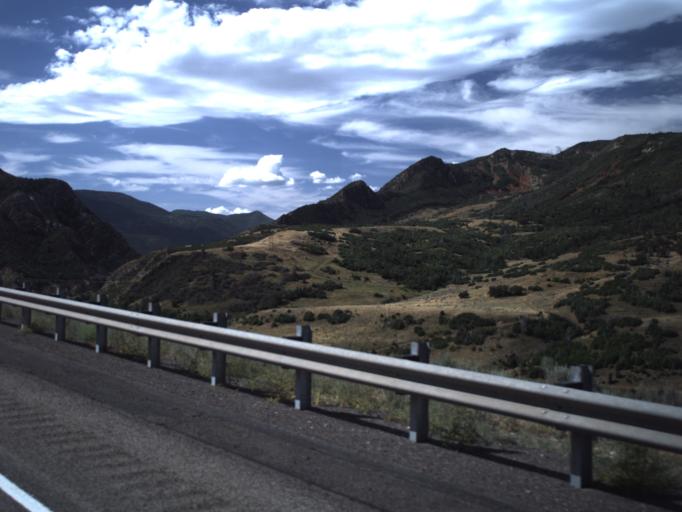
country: US
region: Utah
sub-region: Utah County
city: Mapleton
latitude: 40.0191
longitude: -111.4965
